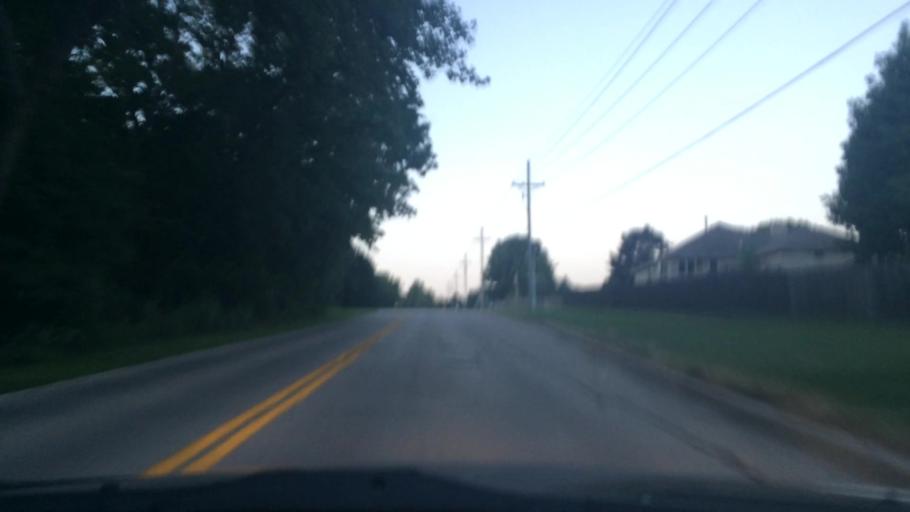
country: US
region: Nebraska
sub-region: Douglas County
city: Ralston
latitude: 41.1945
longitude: -96.0524
